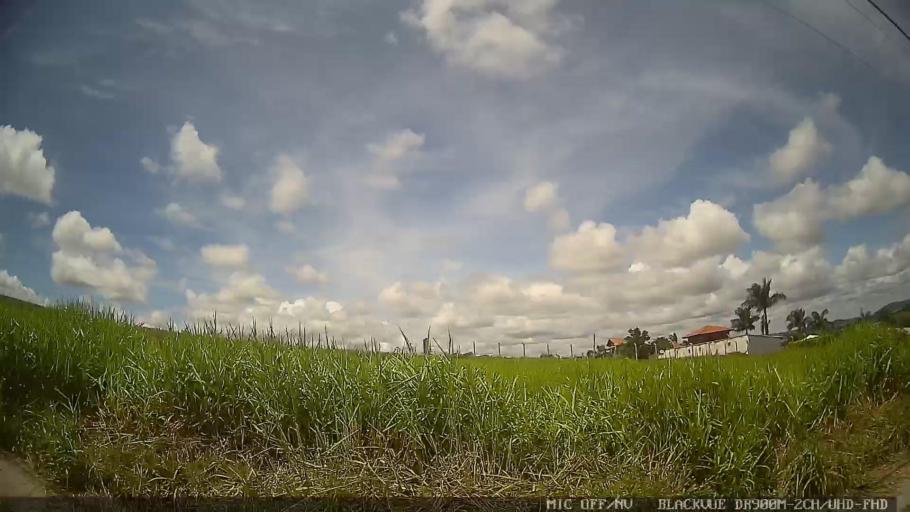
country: BR
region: Sao Paulo
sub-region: Amparo
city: Amparo
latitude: -22.8195
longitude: -46.6935
